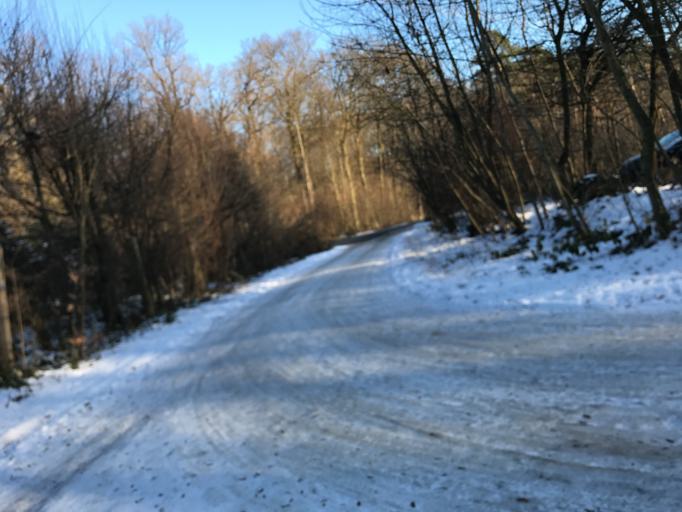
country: DE
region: Hesse
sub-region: Regierungsbezirk Darmstadt
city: Hofheim am Taunus
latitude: 50.0802
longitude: 8.4105
